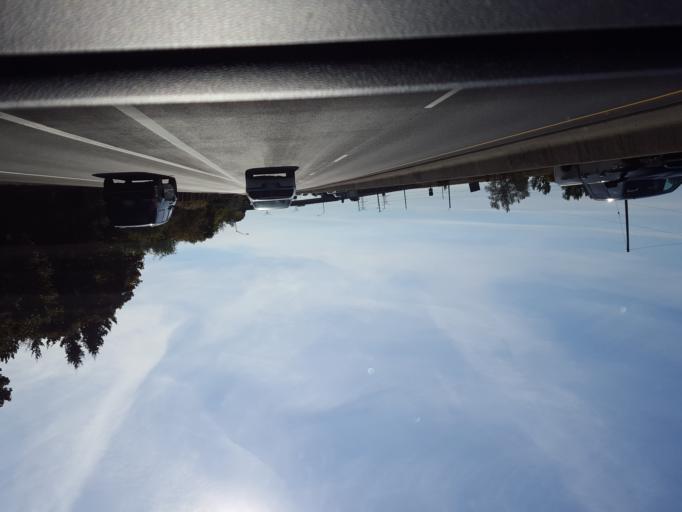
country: CA
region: Ontario
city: Oshawa
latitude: 43.9100
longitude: -78.6179
